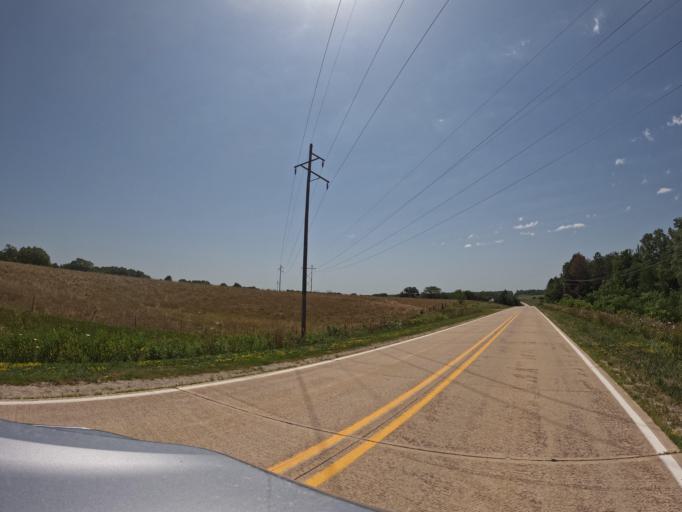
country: US
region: Iowa
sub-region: Henry County
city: Mount Pleasant
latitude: 40.9340
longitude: -91.5545
